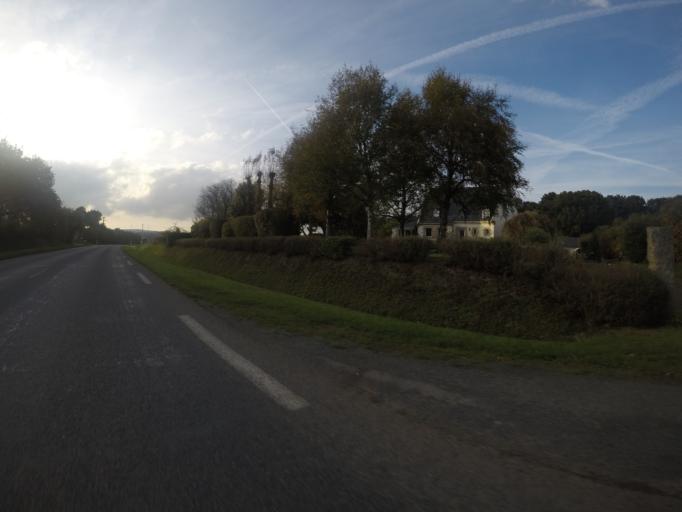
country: FR
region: Brittany
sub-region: Departement des Cotes-d'Armor
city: Graces
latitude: 48.5333
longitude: -3.1939
